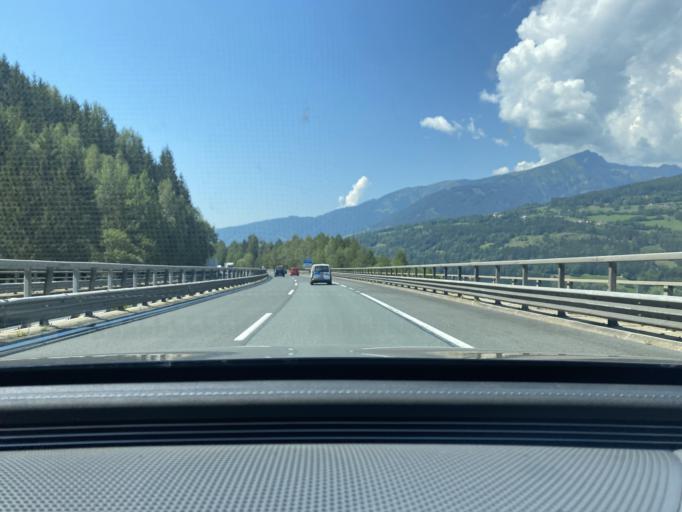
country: AT
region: Carinthia
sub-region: Politischer Bezirk Spittal an der Drau
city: Gmuend
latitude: 46.9086
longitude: 13.5468
